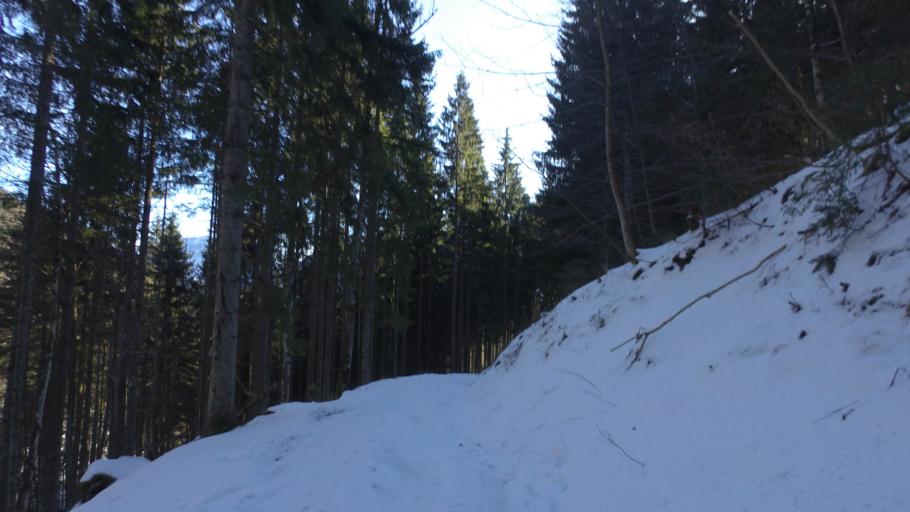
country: DE
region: Bavaria
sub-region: Upper Bavaria
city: Bergen
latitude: 47.7544
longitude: 12.5907
